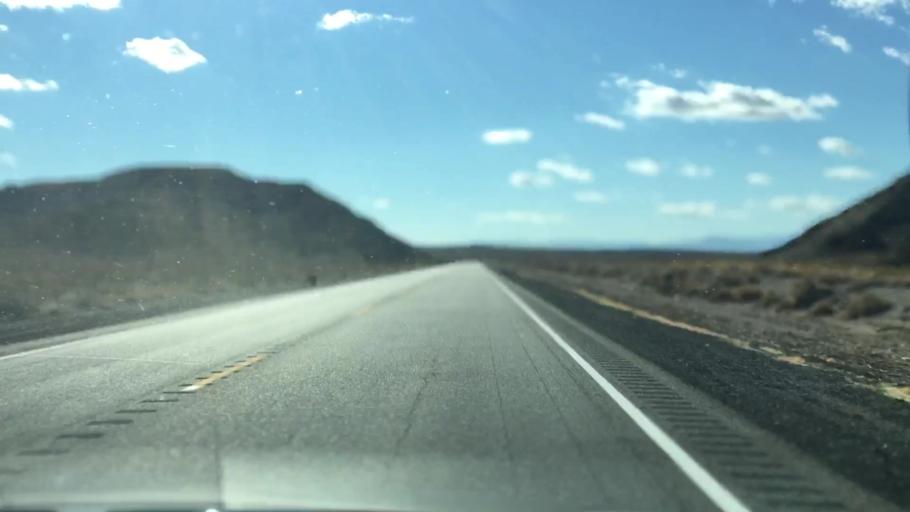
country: US
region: Nevada
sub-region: Nye County
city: Pahrump
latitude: 36.5692
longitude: -116.0797
